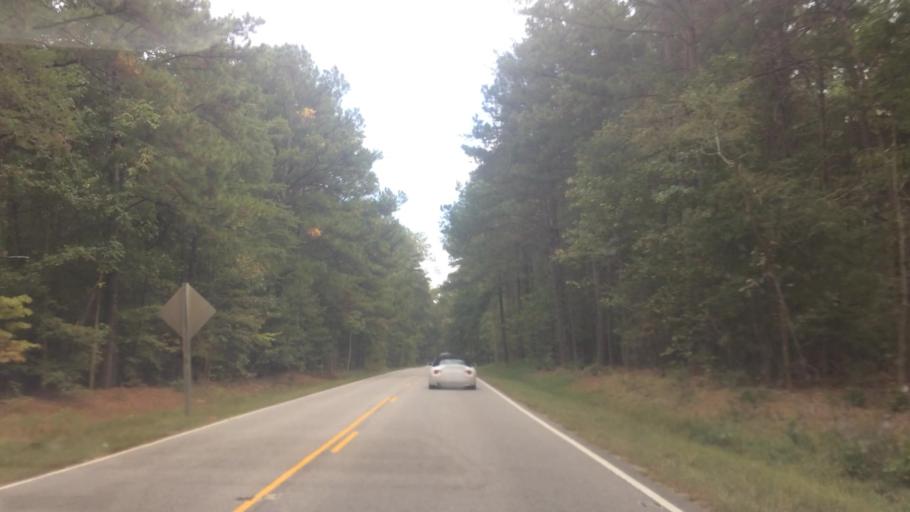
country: US
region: Virginia
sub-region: James City County
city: Williamsburg
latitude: 37.3131
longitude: -76.7278
